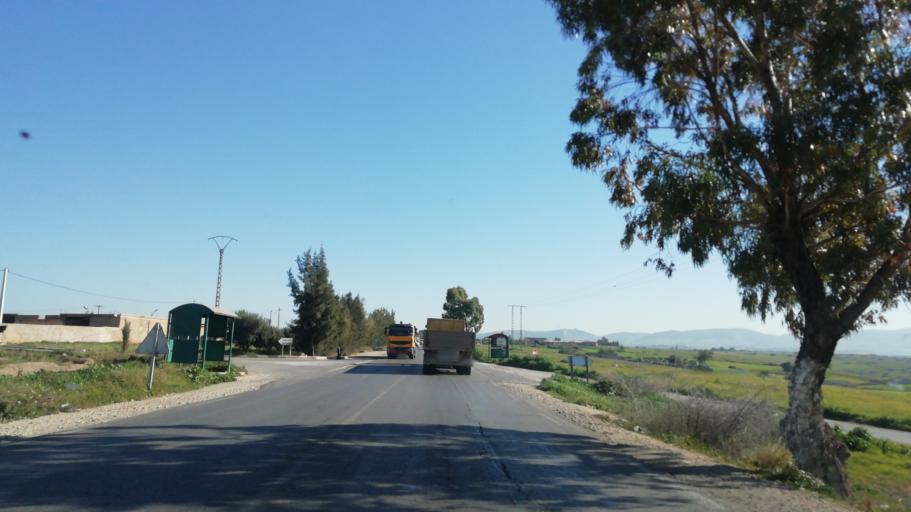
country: DZ
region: Relizane
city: Zemoura
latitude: 35.7511
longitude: 0.6873
